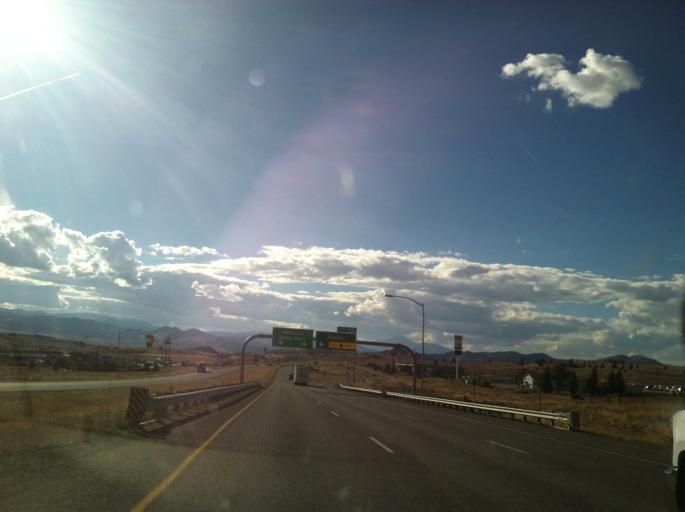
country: US
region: Montana
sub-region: Silver Bow County
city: Butte
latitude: 46.0065
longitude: -112.6026
